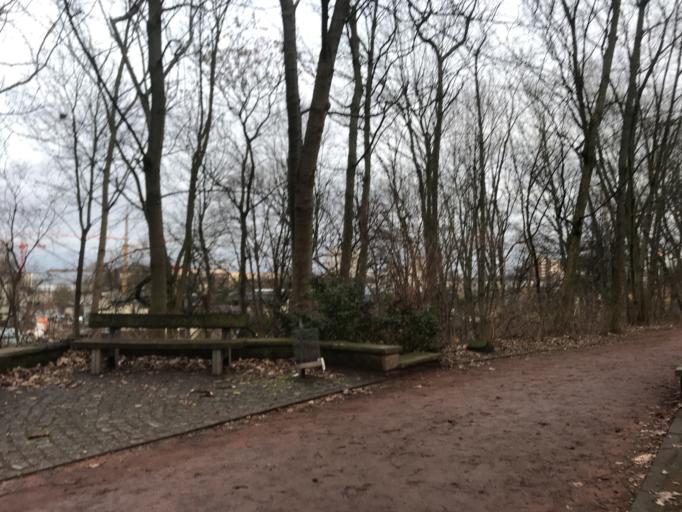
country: DE
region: Berlin
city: Tiergarten Bezirk
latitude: 52.5284
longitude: 13.3572
